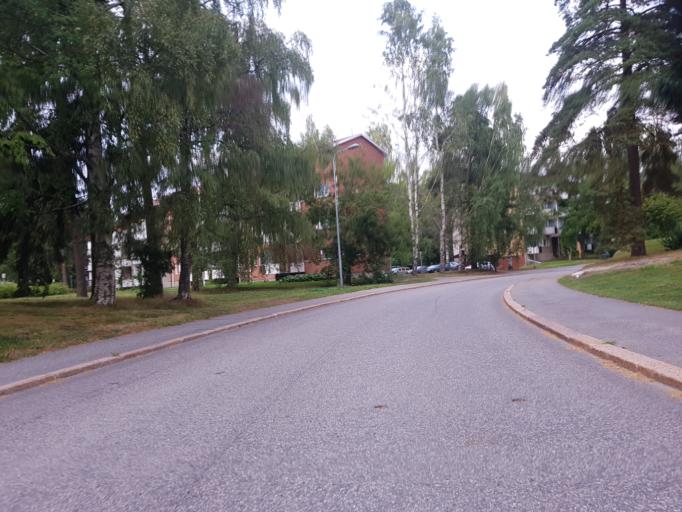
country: FI
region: Uusimaa
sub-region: Helsinki
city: Helsinki
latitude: 60.2290
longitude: 24.9505
